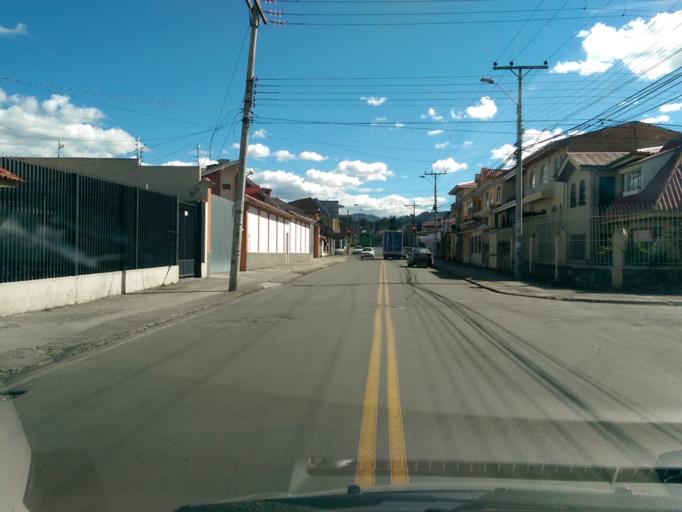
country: EC
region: Azuay
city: Cuenca
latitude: -2.9017
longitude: -79.0194
